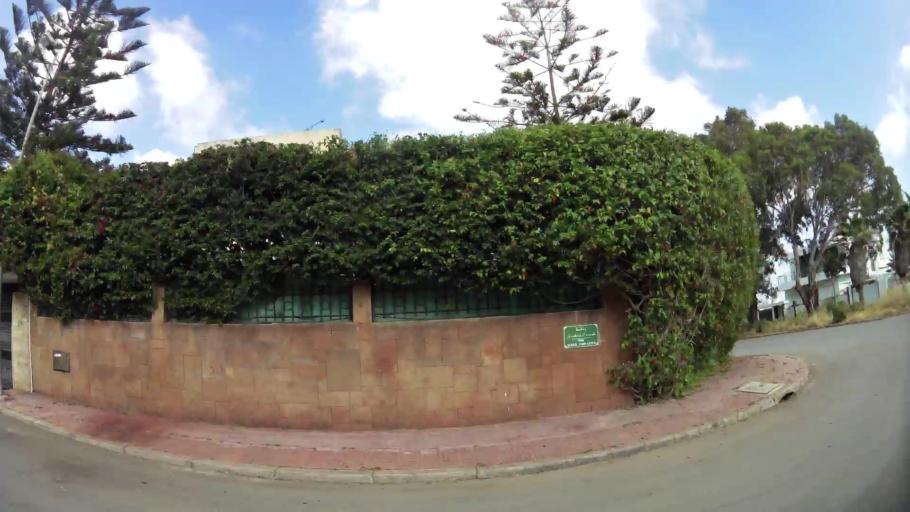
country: MA
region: Rabat-Sale-Zemmour-Zaer
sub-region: Skhirate-Temara
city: Temara
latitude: 33.9541
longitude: -6.8780
